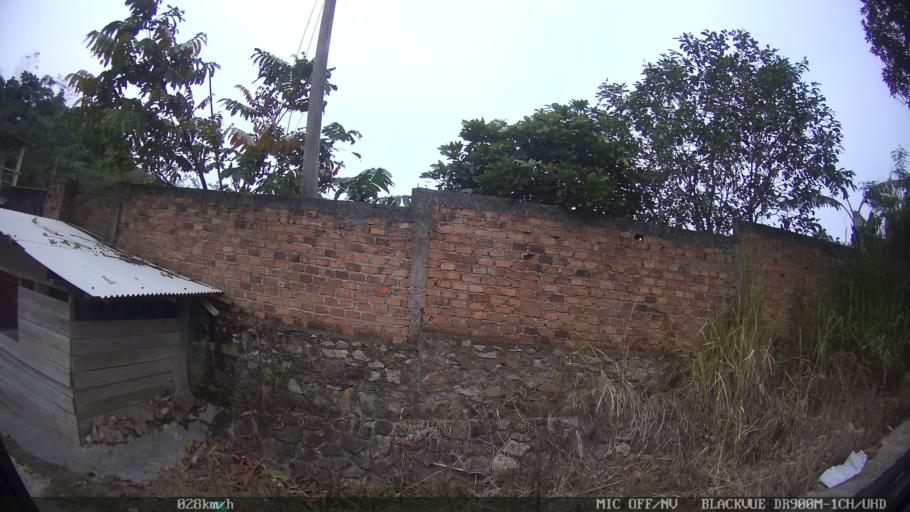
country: ID
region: Lampung
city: Panjang
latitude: -5.4389
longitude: 105.3127
